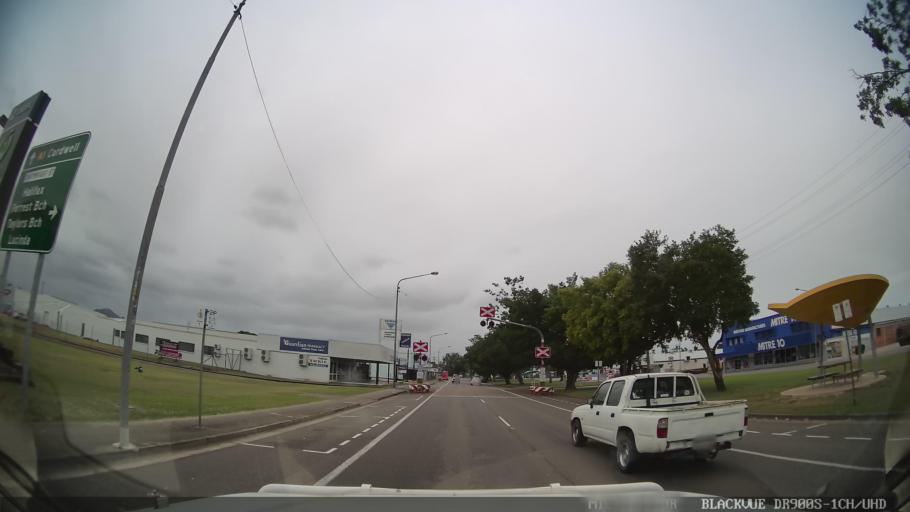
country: AU
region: Queensland
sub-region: Hinchinbrook
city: Ingham
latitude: -18.6473
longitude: 146.1605
